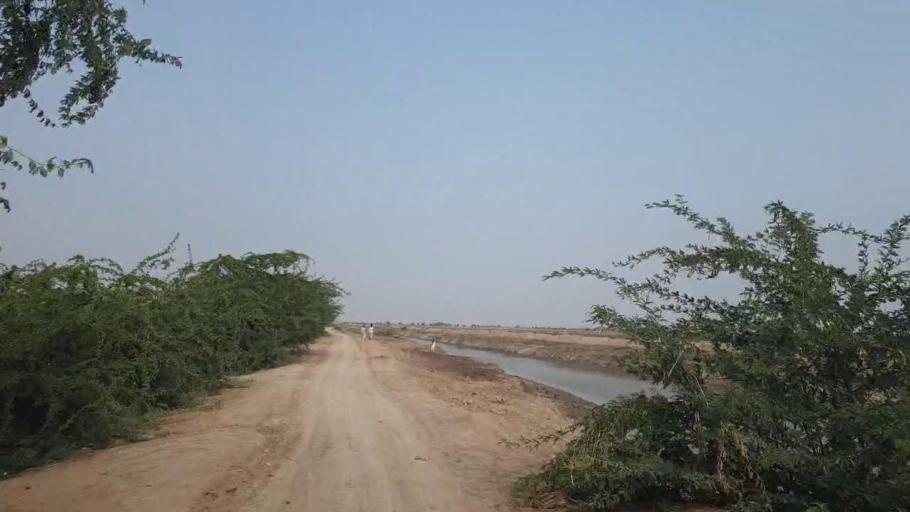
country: PK
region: Sindh
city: Badin
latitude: 24.7180
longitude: 68.7710
